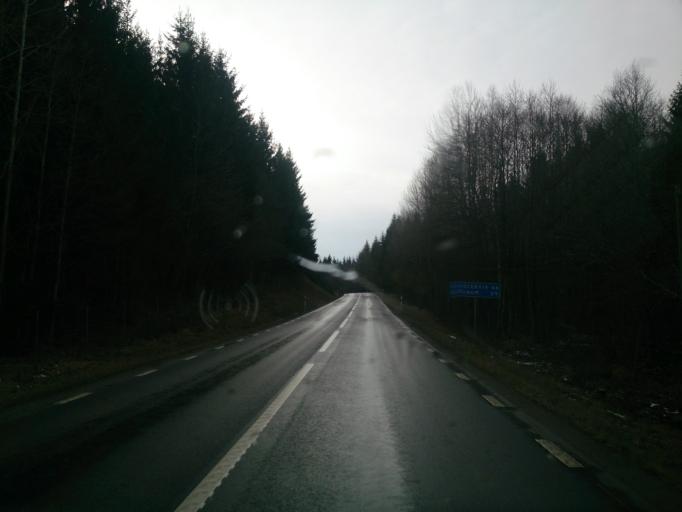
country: SE
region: OEstergoetland
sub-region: Atvidabergs Kommun
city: Atvidaberg
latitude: 58.1791
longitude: 16.0258
